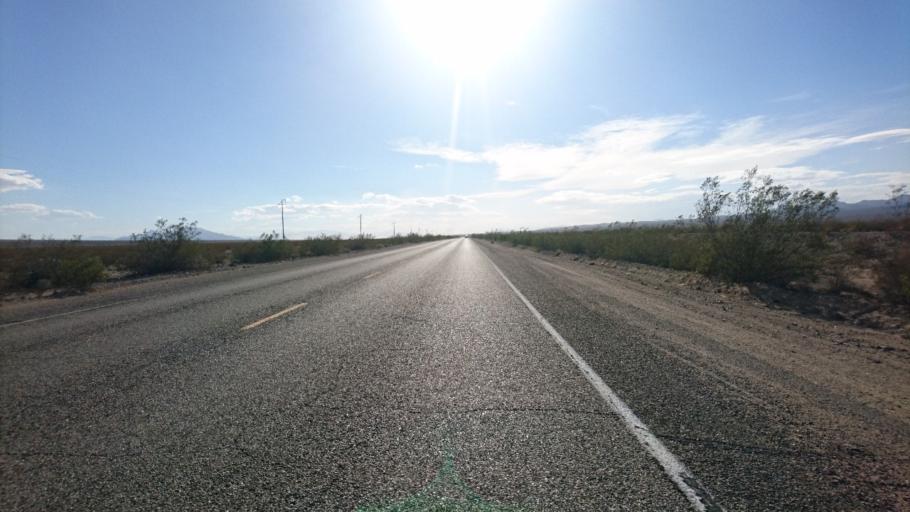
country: US
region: California
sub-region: San Bernardino County
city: Needles
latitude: 34.7097
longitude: -115.2850
